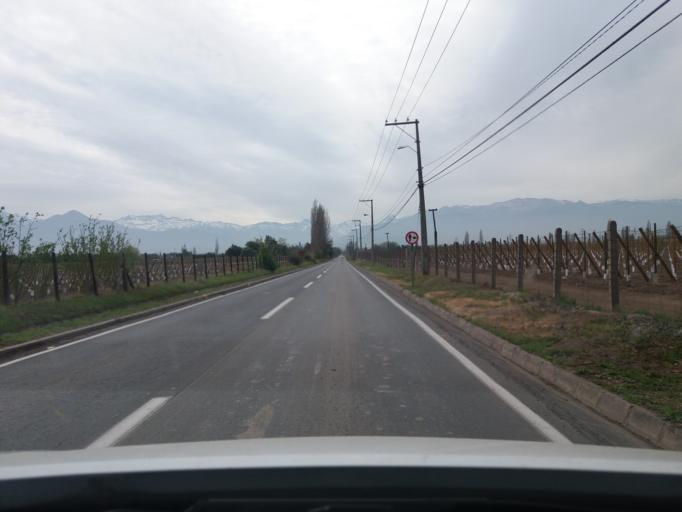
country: CL
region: Valparaiso
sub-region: Provincia de Los Andes
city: Los Andes
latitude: -32.8213
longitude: -70.6737
